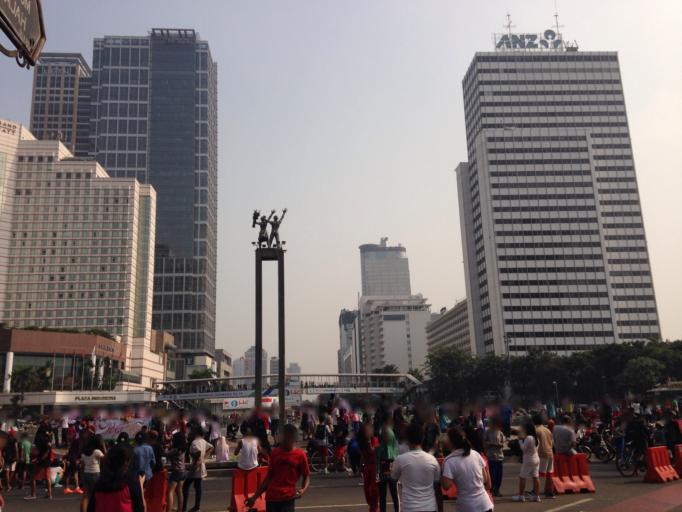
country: ID
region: Jakarta Raya
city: Jakarta
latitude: -6.1956
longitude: 106.8231
